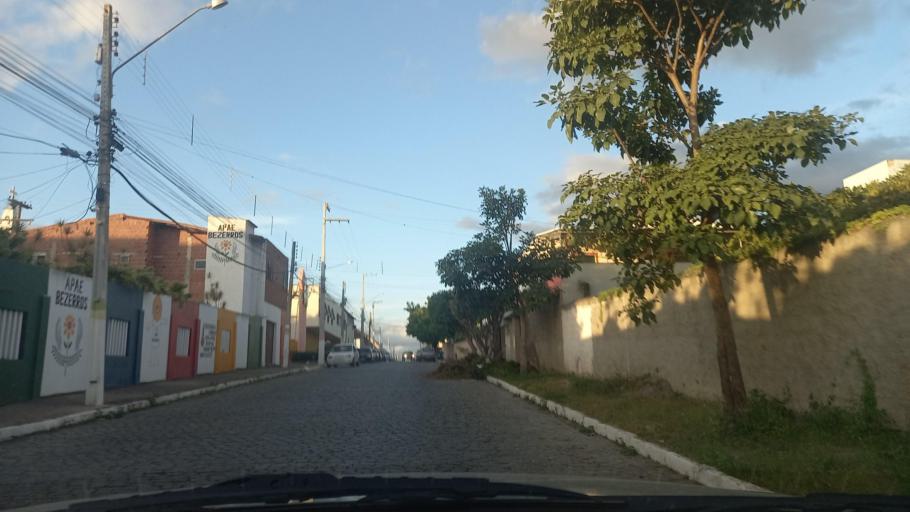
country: BR
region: Pernambuco
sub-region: Bezerros
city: Bezerros
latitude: -8.2422
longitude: -35.7531
